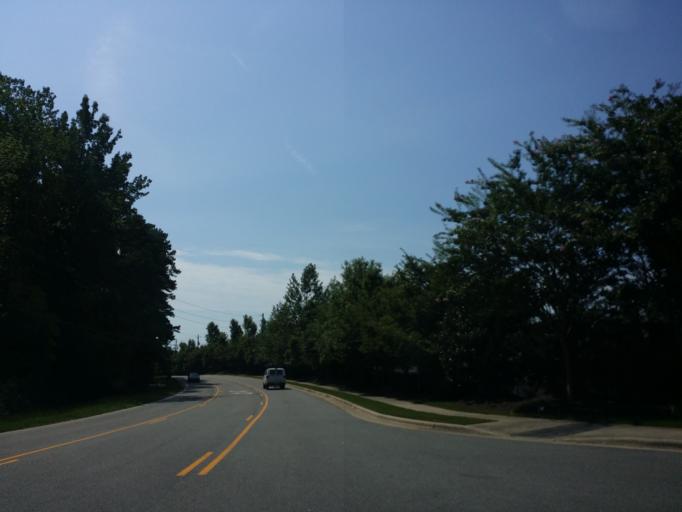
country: US
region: North Carolina
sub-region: Wake County
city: Cary
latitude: 35.8876
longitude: -78.7275
